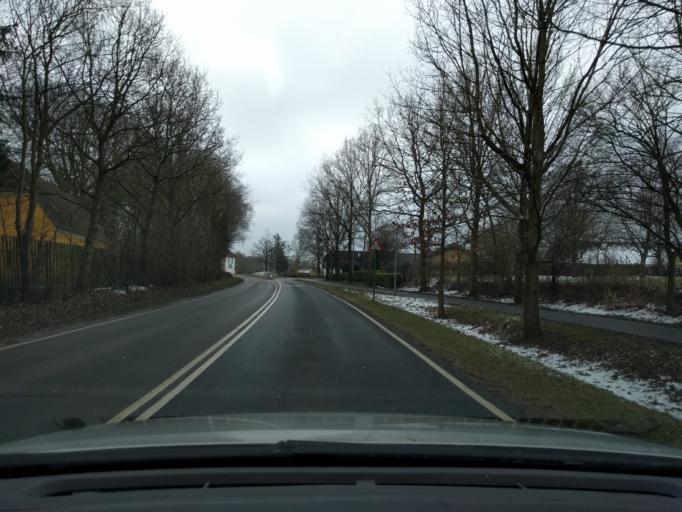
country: DK
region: South Denmark
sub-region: Odense Kommune
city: Bellinge
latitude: 55.3700
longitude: 10.3278
